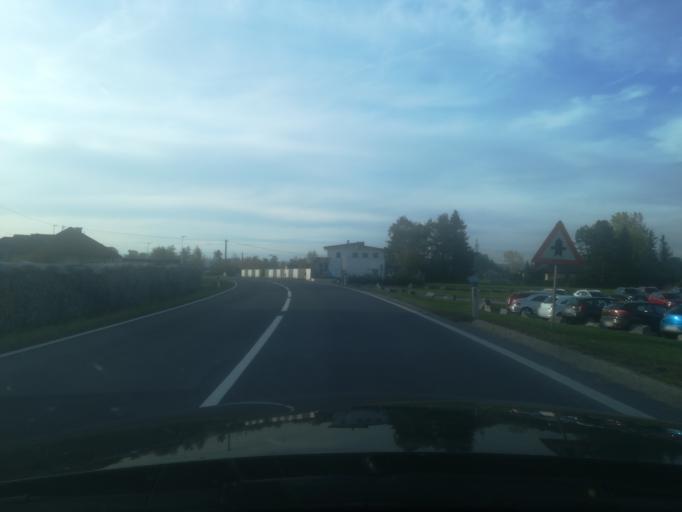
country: AT
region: Upper Austria
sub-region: Wels-Land
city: Gunskirchen
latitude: 48.1371
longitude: 13.9484
